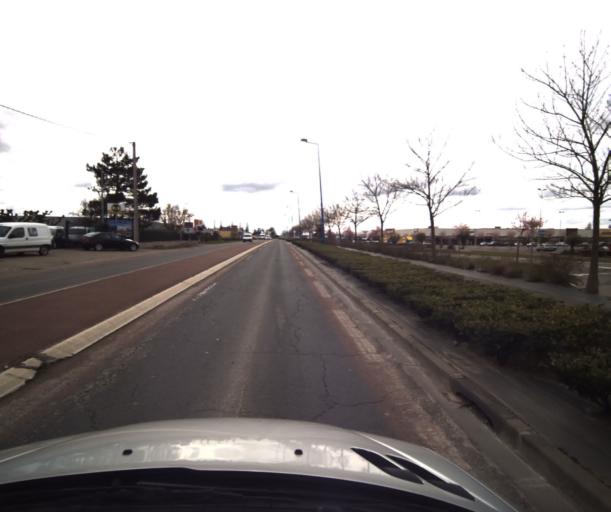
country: FR
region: Midi-Pyrenees
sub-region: Departement du Tarn-et-Garonne
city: Montauban
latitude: 44.0414
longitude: 1.3853
